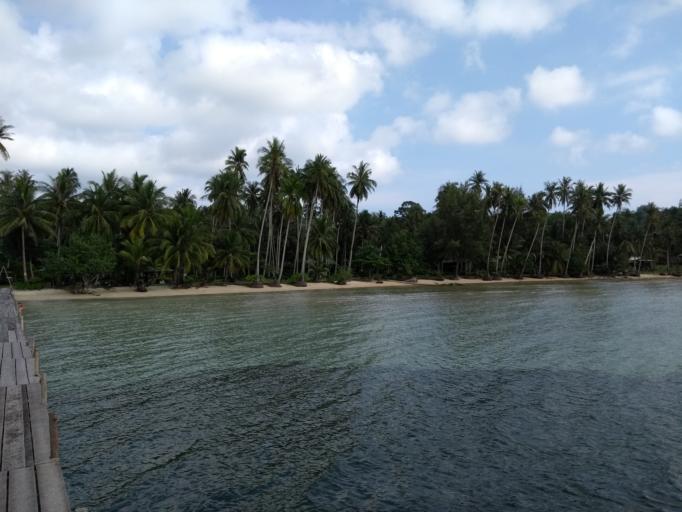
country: TH
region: Trat
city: Ko Kut
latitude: 11.6225
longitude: 102.5446
